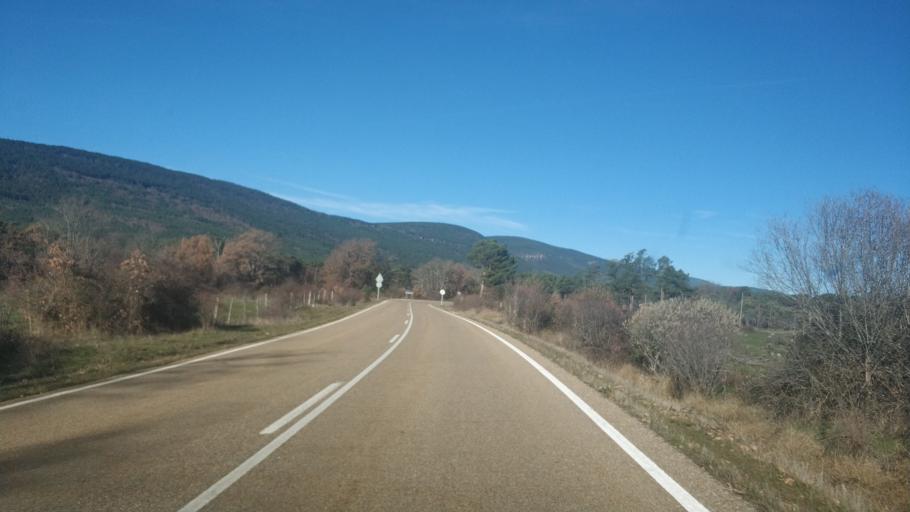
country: ES
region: Castille and Leon
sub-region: Provincia de Soria
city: Vinuesa
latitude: 41.9203
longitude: -2.7589
